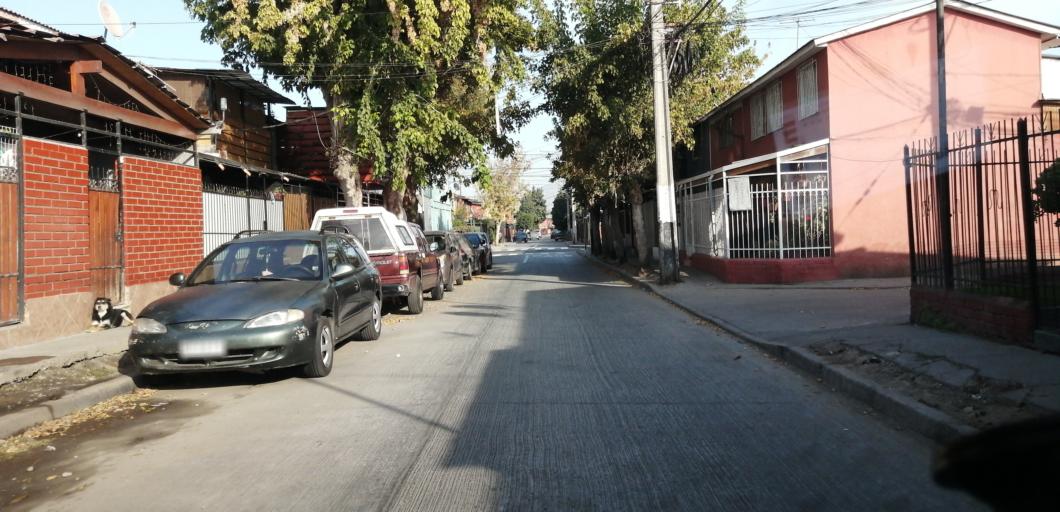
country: CL
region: Santiago Metropolitan
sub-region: Provincia de Santiago
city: Lo Prado
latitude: -33.4613
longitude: -70.7559
